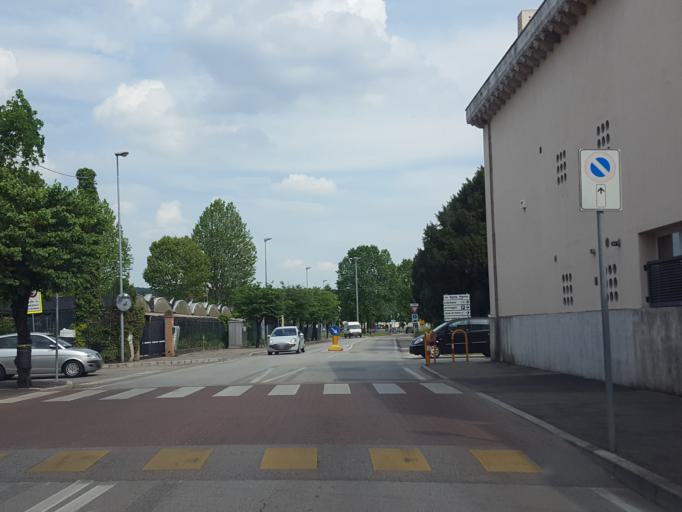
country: IT
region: Veneto
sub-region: Provincia di Vicenza
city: Lonigo
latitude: 45.3827
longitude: 11.3926
